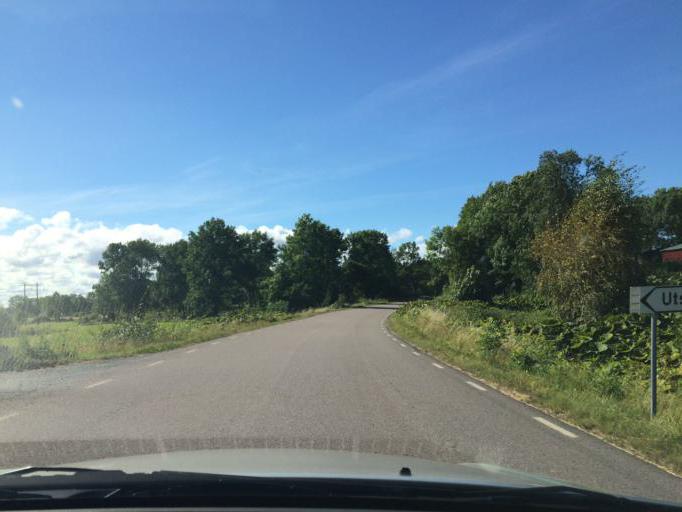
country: SE
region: Soedermanland
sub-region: Eskilstuna Kommun
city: Torshalla
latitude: 59.5252
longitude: 16.4414
